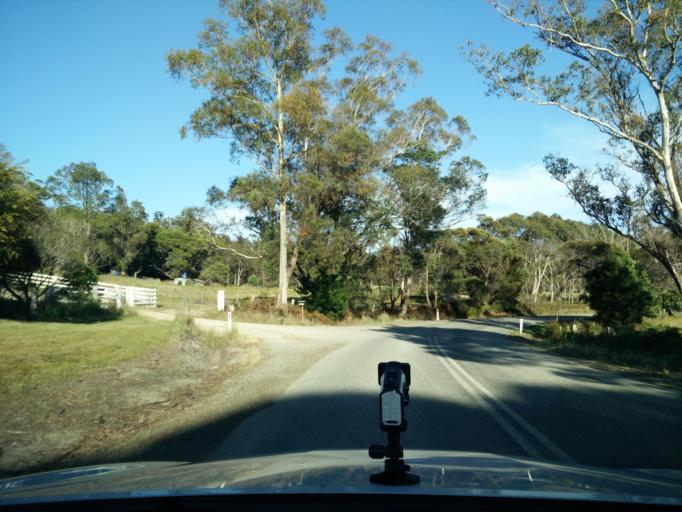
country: AU
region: Tasmania
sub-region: Break O'Day
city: St Helens
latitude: -41.2611
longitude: 148.0885
